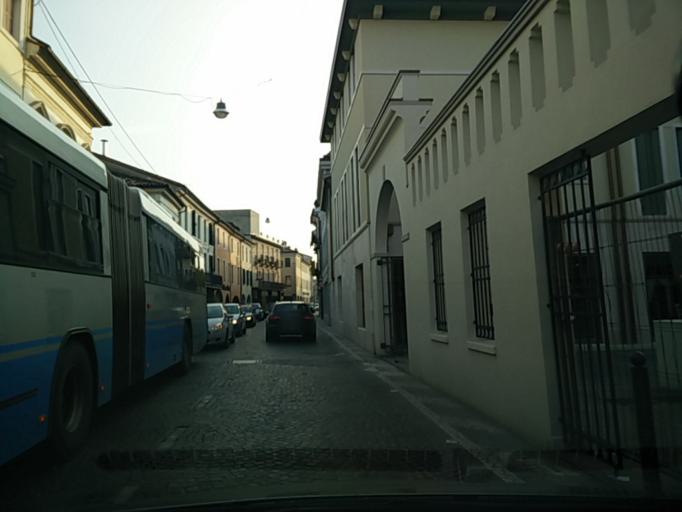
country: IT
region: Veneto
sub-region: Provincia di Treviso
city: Castelfranco Veneto
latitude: 45.6744
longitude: 11.9273
